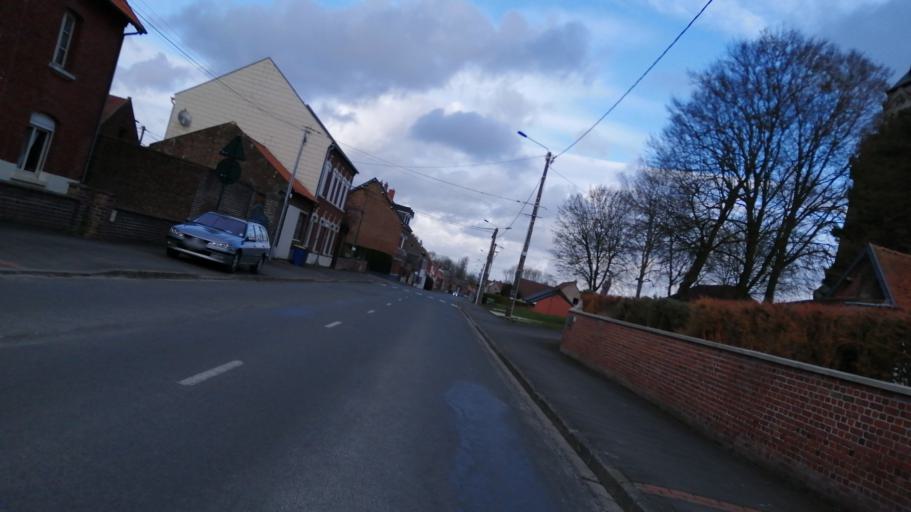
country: FR
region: Nord-Pas-de-Calais
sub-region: Departement du Pas-de-Calais
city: Tilloy-les-Mofflaines
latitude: 50.2469
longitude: 2.8192
